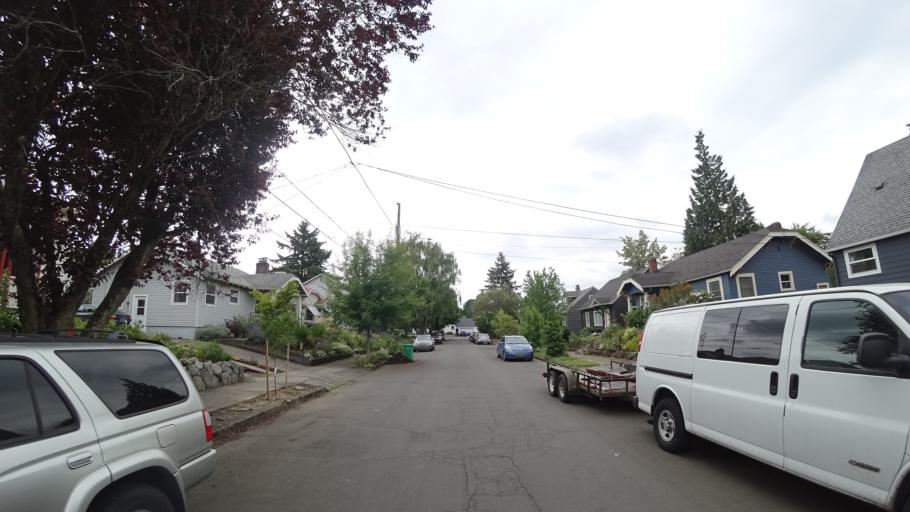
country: US
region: Oregon
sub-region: Clackamas County
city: Milwaukie
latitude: 45.4911
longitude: -122.6347
